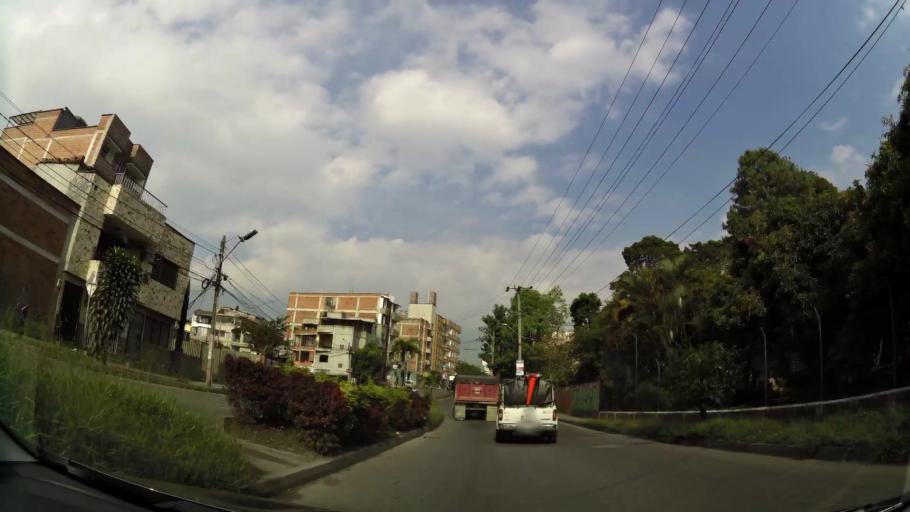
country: CO
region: Antioquia
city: Sabaneta
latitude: 6.1686
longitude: -75.6223
